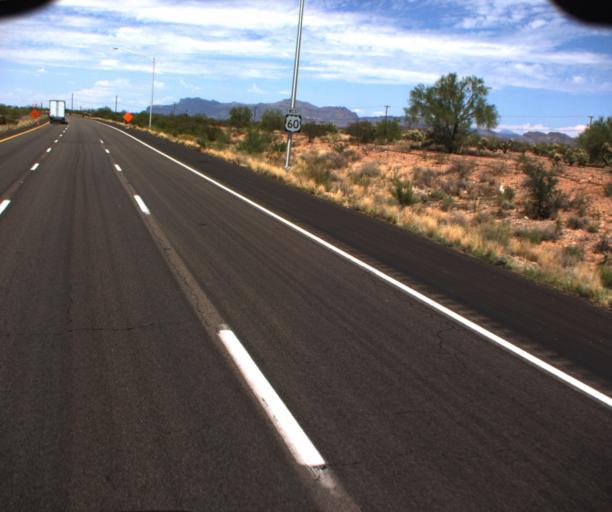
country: US
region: Arizona
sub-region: Pinal County
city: Gold Camp
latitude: 33.2614
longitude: -111.3446
